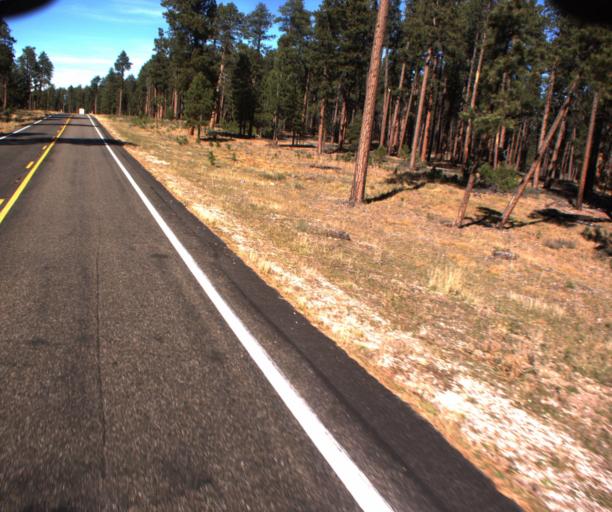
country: US
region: Arizona
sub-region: Coconino County
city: Fredonia
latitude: 36.6598
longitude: -112.1897
